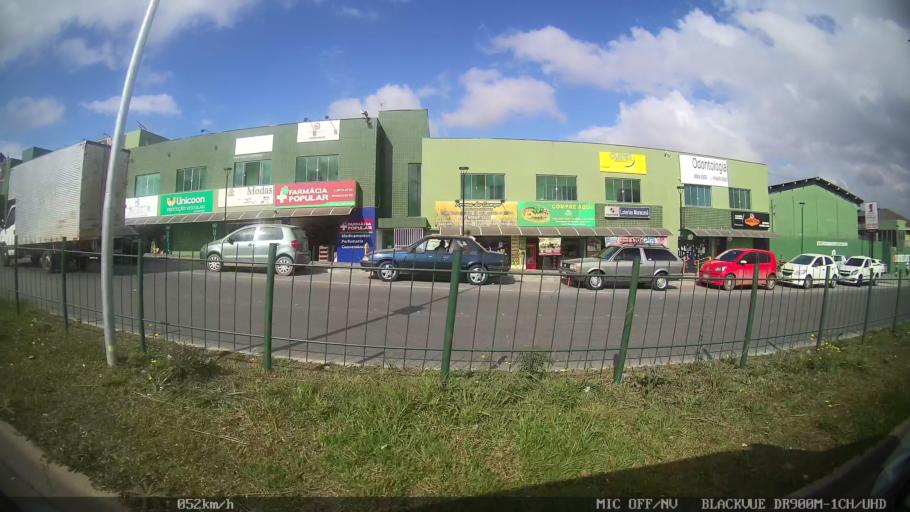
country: BR
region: Parana
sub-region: Pinhais
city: Pinhais
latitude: -25.3866
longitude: -49.1894
